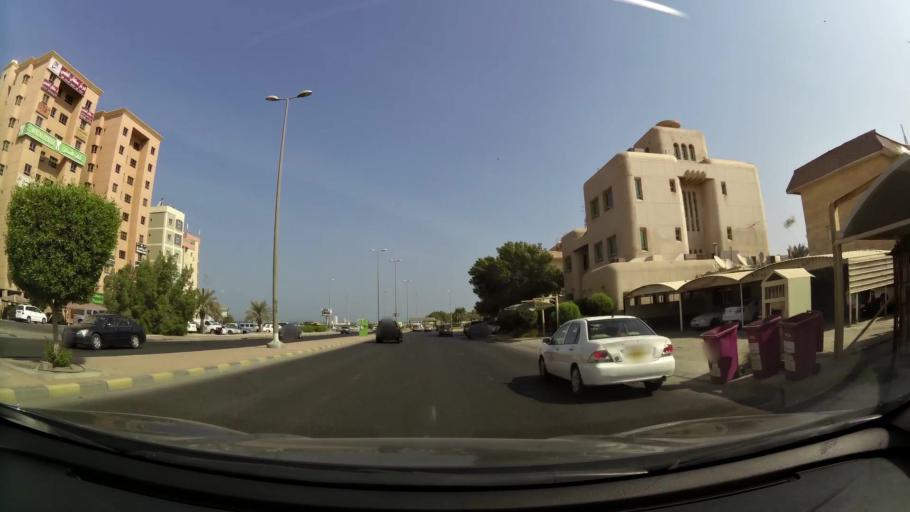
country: KW
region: Al Ahmadi
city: Al Manqaf
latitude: 29.0920
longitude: 48.1358
